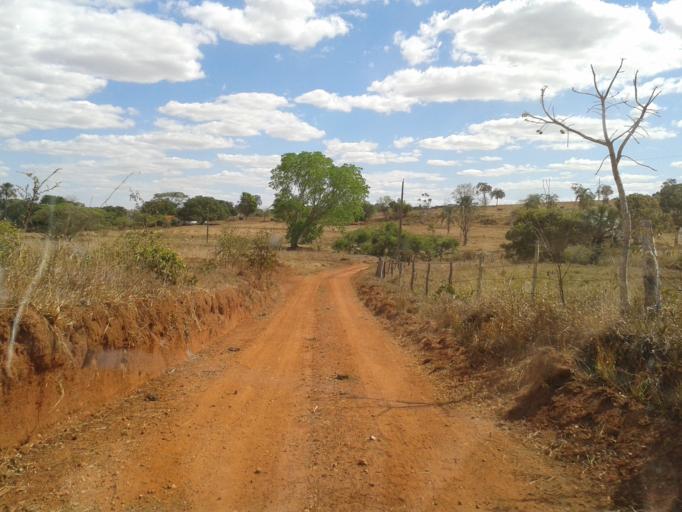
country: BR
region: Minas Gerais
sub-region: Monte Alegre De Minas
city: Monte Alegre de Minas
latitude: -18.7952
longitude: -49.0931
